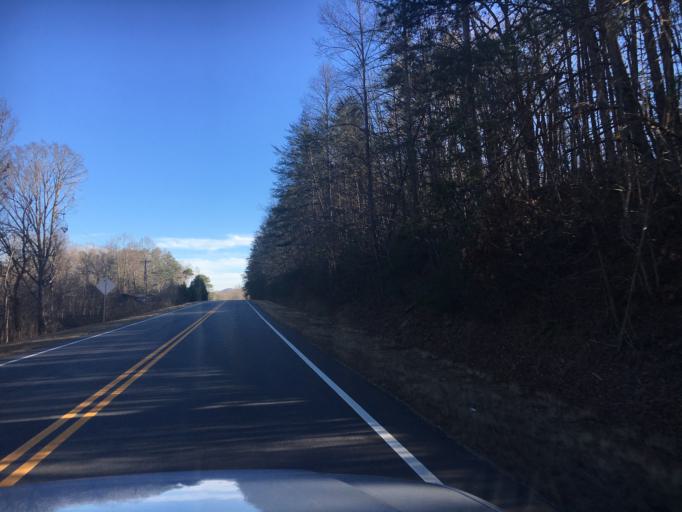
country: US
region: Georgia
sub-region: White County
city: Cleveland
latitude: 34.6434
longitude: -83.8385
